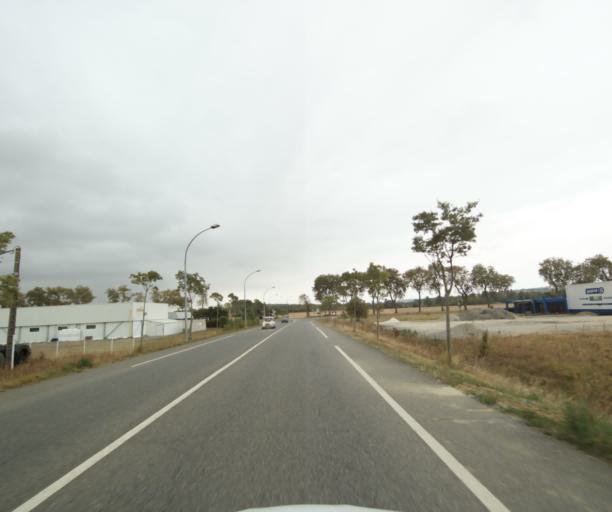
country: FR
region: Midi-Pyrenees
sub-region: Departement de la Haute-Garonne
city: Villefranche-de-Lauragais
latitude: 43.3983
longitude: 1.7035
